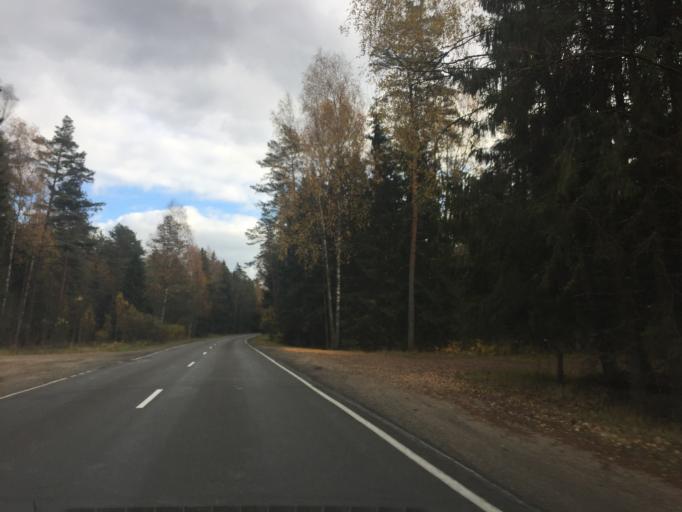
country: BY
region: Minsk
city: Svir
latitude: 54.9247
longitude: 26.5011
